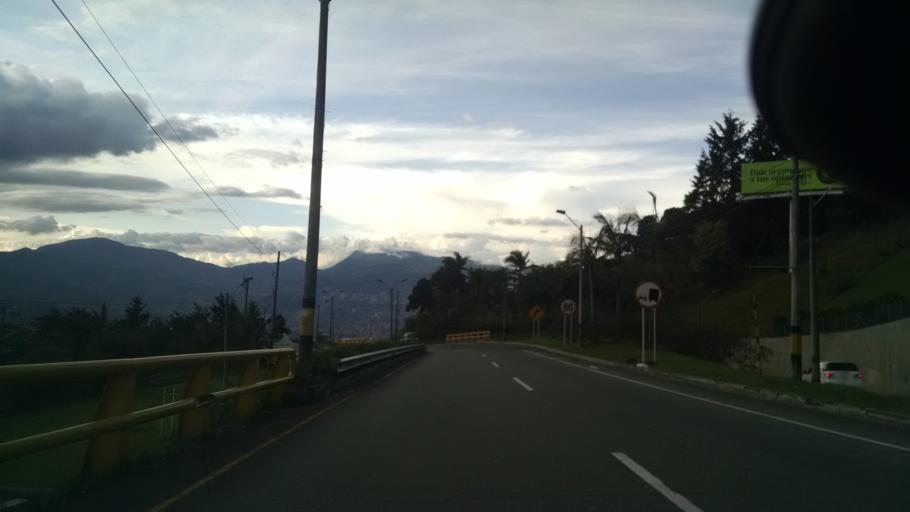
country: CO
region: Antioquia
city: Envigado
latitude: 6.1846
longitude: -75.5455
